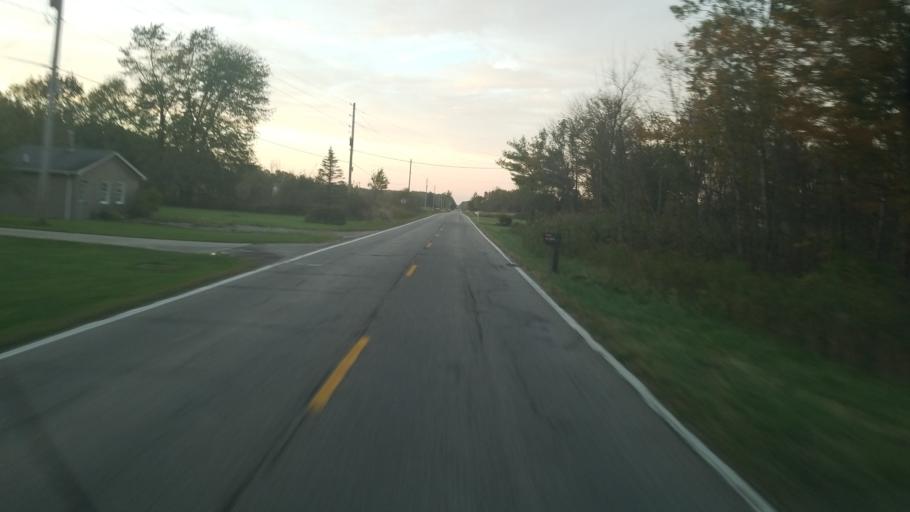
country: US
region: Ohio
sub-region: Ashtabula County
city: Andover
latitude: 41.6366
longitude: -80.6668
